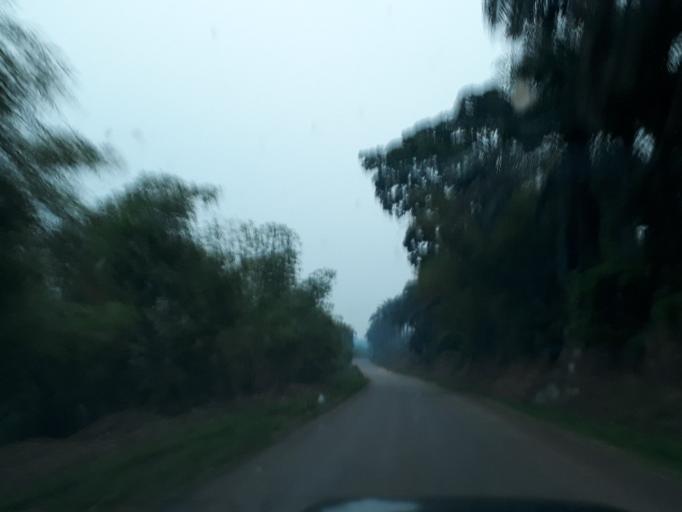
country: CD
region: Bandundu
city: Kikwit
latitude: -5.0781
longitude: 18.8820
